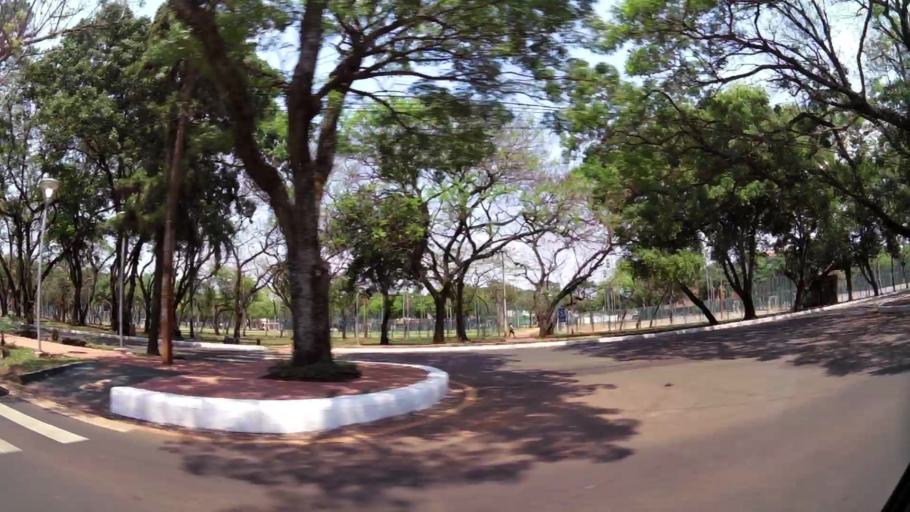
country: PY
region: Alto Parana
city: Ciudad del Este
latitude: -25.5167
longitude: -54.6138
